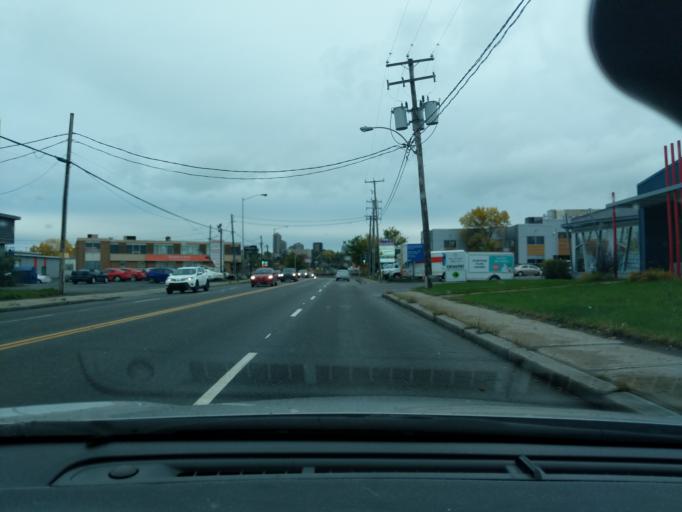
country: CA
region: Quebec
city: Quebec
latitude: 46.8051
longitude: -71.2654
